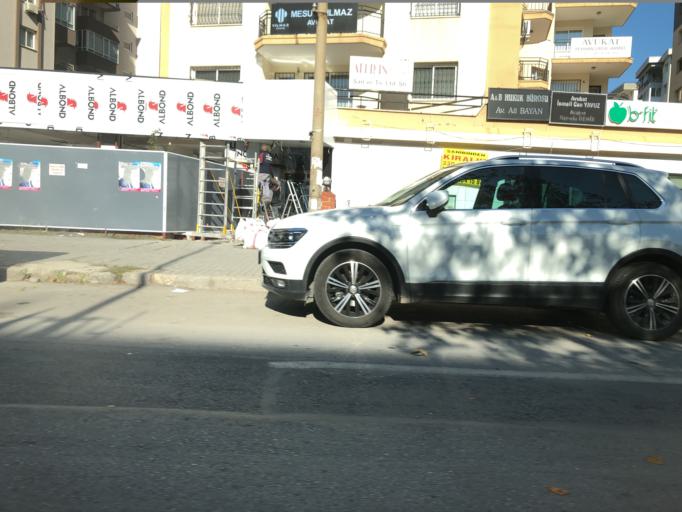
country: TR
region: Izmir
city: Buca
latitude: 38.4559
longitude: 27.1803
